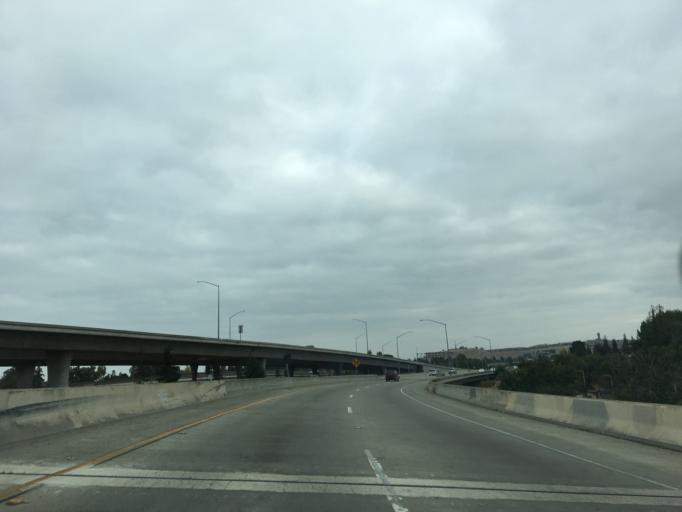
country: US
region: California
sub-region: Santa Clara County
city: Seven Trees
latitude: 37.2575
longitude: -121.8581
